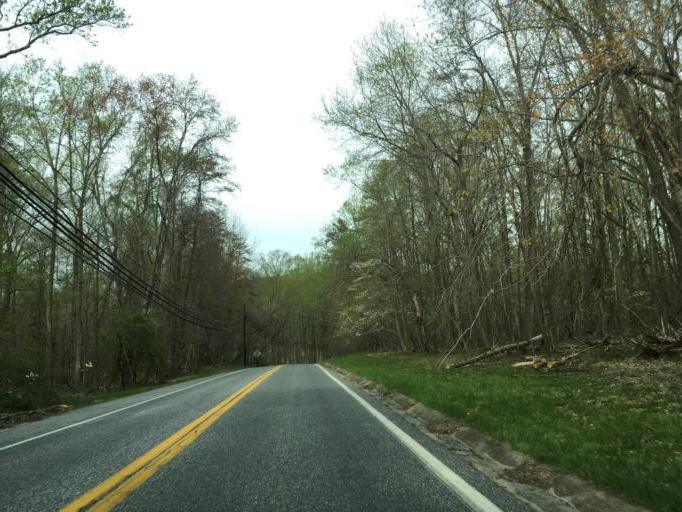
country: US
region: Maryland
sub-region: Baltimore County
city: Hunt Valley
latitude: 39.4931
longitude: -76.6056
